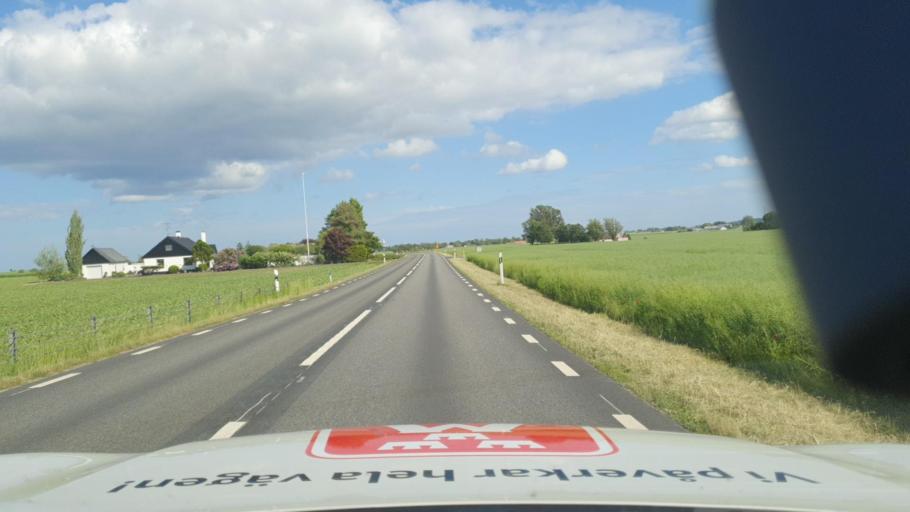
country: SE
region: Skane
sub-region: Simrishamns Kommun
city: Simrishamn
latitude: 55.5406
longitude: 14.2107
